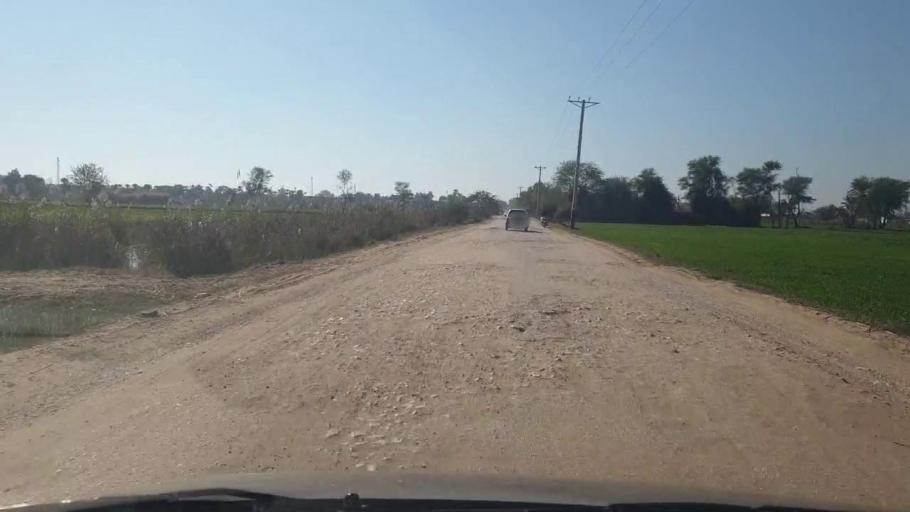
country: PK
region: Sindh
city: Bozdar
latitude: 27.0781
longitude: 68.6174
